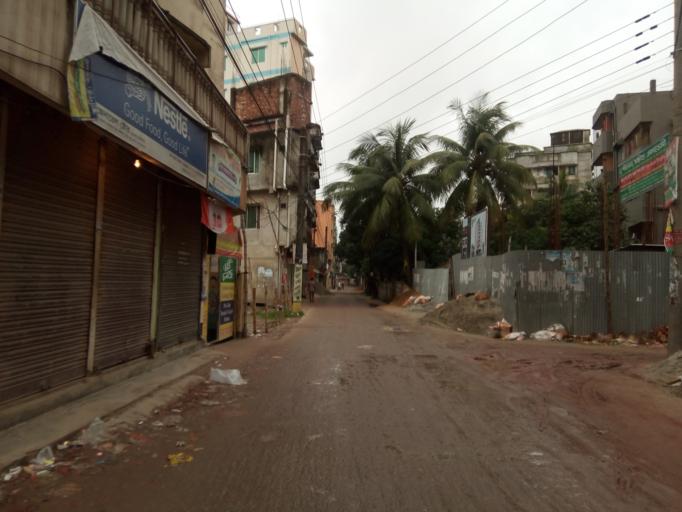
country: BD
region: Dhaka
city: Tungi
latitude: 23.8473
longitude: 90.4217
